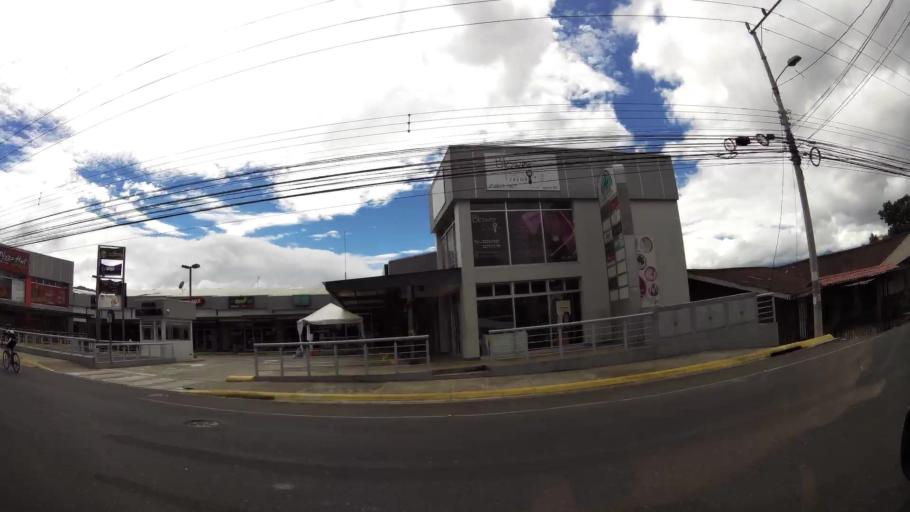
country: CR
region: Cartago
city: San Diego
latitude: 9.9095
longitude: -84.0110
